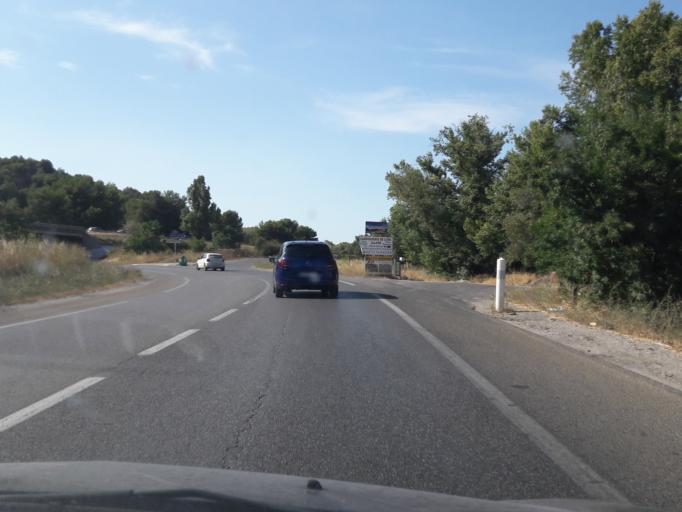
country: FR
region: Provence-Alpes-Cote d'Azur
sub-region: Departement des Bouches-du-Rhone
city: Bouc-Bel-Air
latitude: 43.4888
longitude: 5.4089
